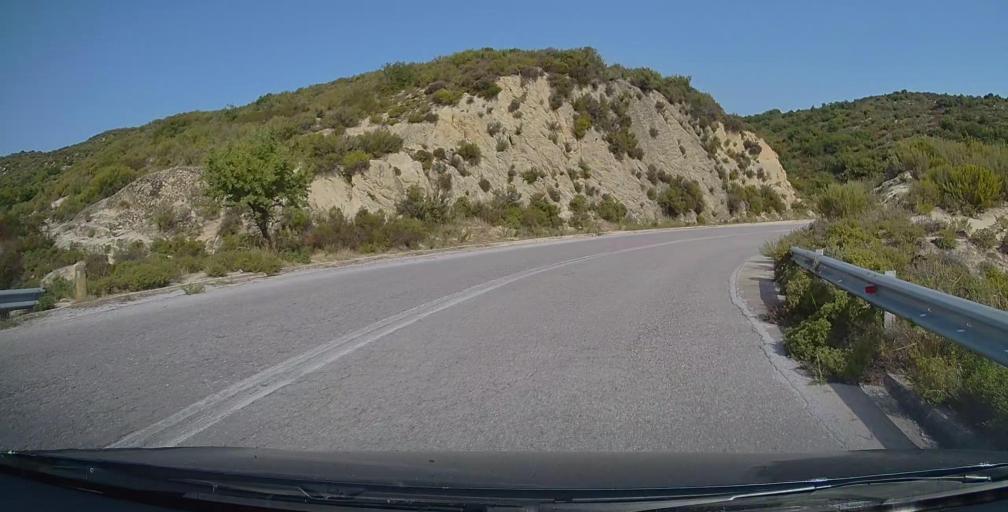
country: GR
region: Central Macedonia
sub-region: Nomos Chalkidikis
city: Sykia
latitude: 39.9931
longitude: 23.9559
